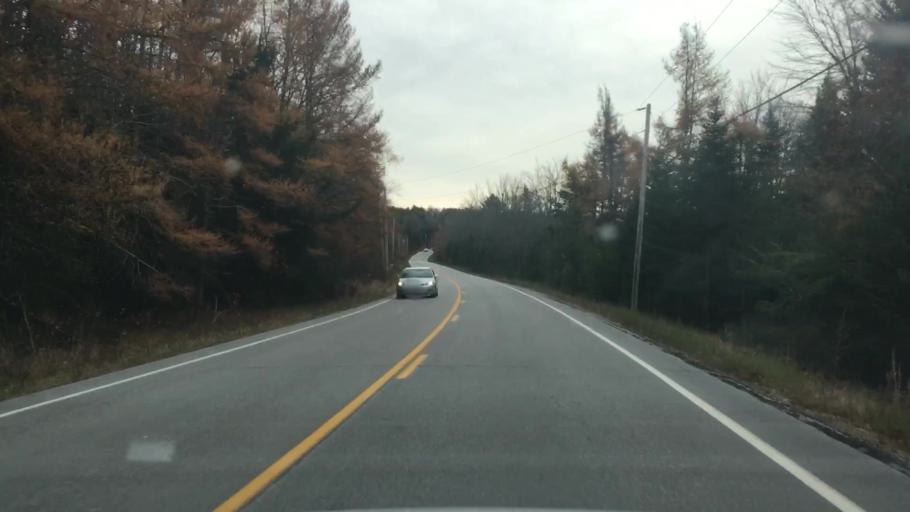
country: US
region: Maine
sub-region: Hancock County
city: Penobscot
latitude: 44.5031
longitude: -68.6542
